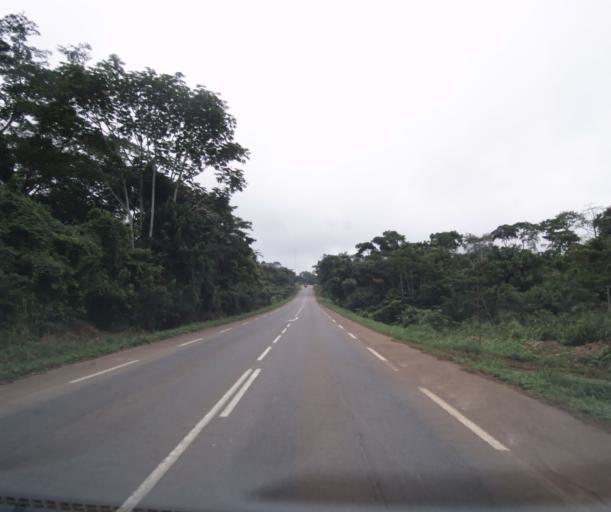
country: CM
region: Centre
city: Mbankomo
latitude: 3.7655
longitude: 11.1217
